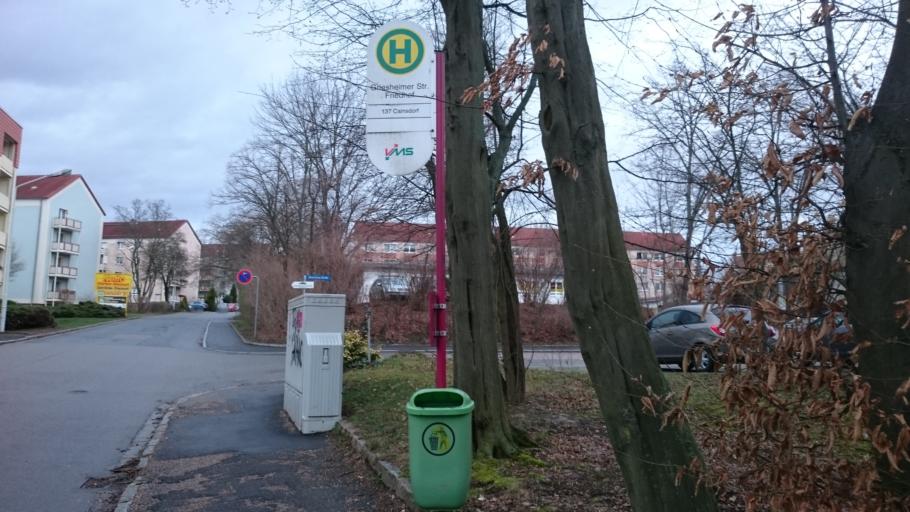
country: DE
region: Saxony
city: Wilkau-Hasslau
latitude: 50.6821
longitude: 12.5074
